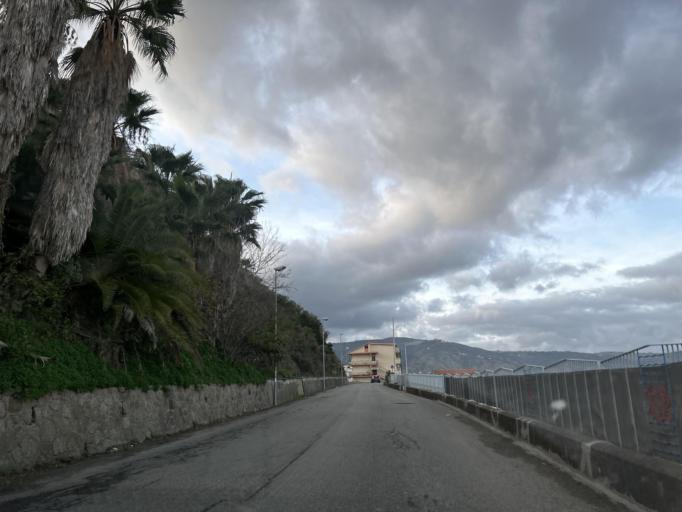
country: IT
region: Calabria
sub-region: Provincia di Catanzaro
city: Soverato Superiore
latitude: 38.6953
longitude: 16.5434
